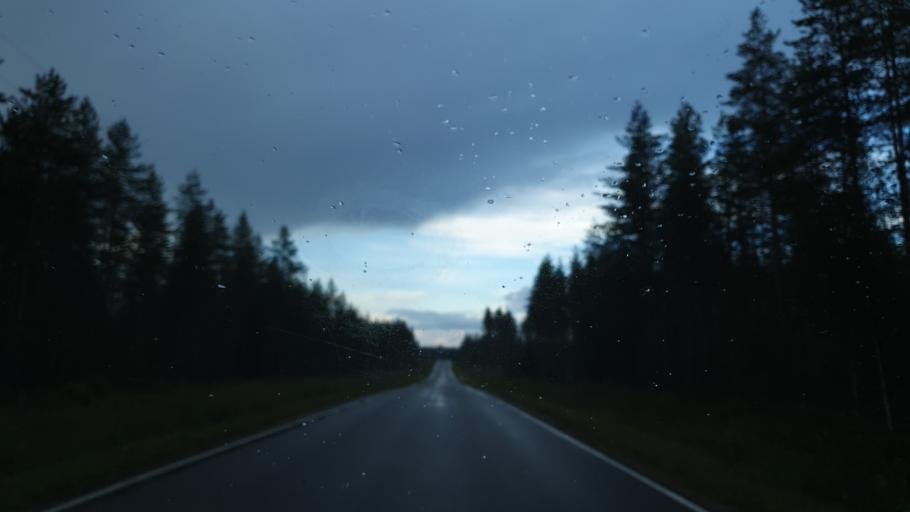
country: FI
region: North Karelia
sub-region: Pielisen Karjala
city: Lieksa
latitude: 63.6568
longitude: 29.8621
